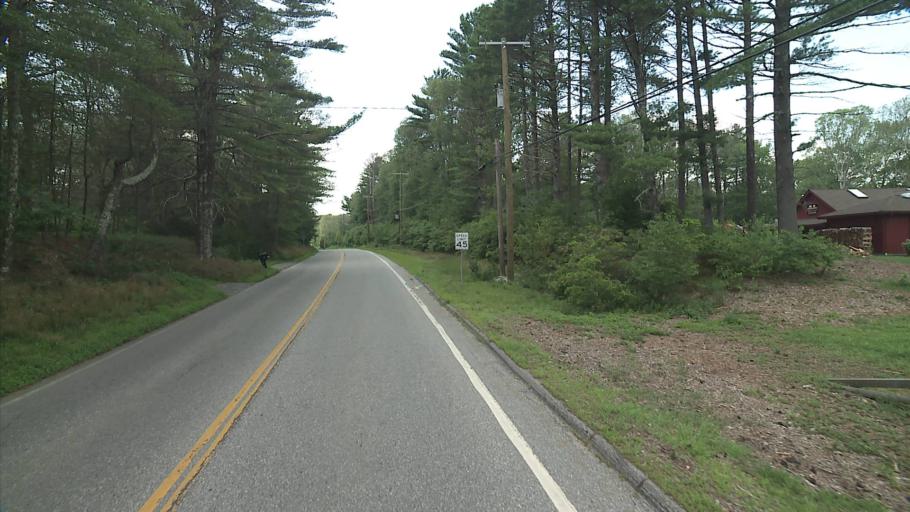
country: US
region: Rhode Island
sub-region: Washington County
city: Hope Valley
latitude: 41.5761
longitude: -71.8090
